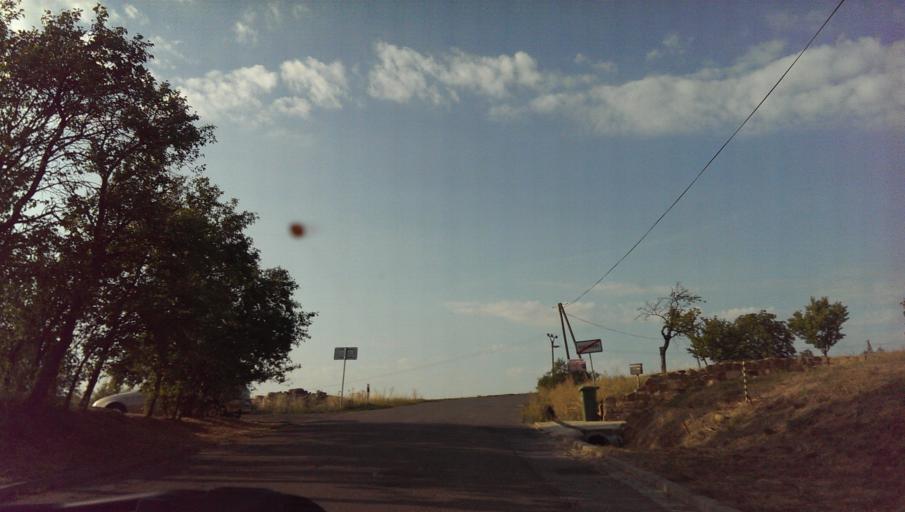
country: CZ
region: South Moravian
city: Zeravice
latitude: 49.0559
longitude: 17.2468
